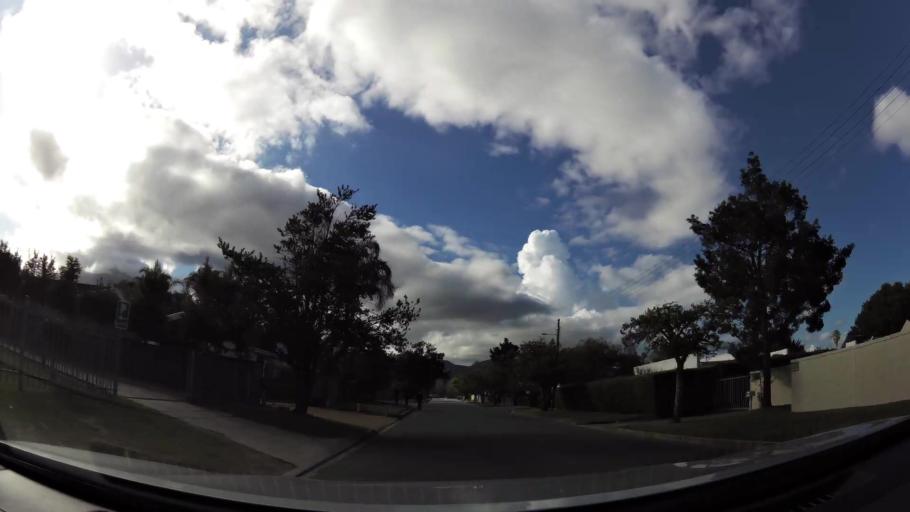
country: ZA
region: Western Cape
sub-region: Eden District Municipality
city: George
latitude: -33.9616
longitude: 22.4808
